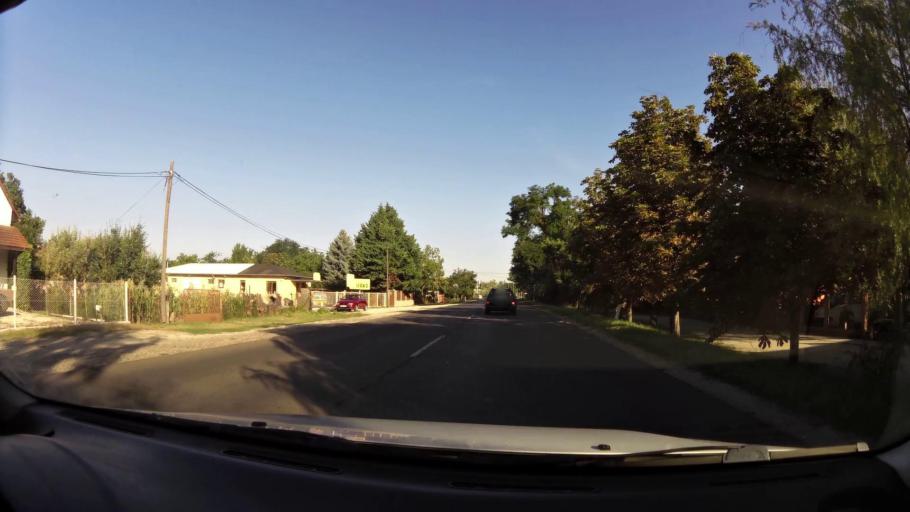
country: HU
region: Pest
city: Nyaregyhaza
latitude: 47.3064
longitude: 19.5046
